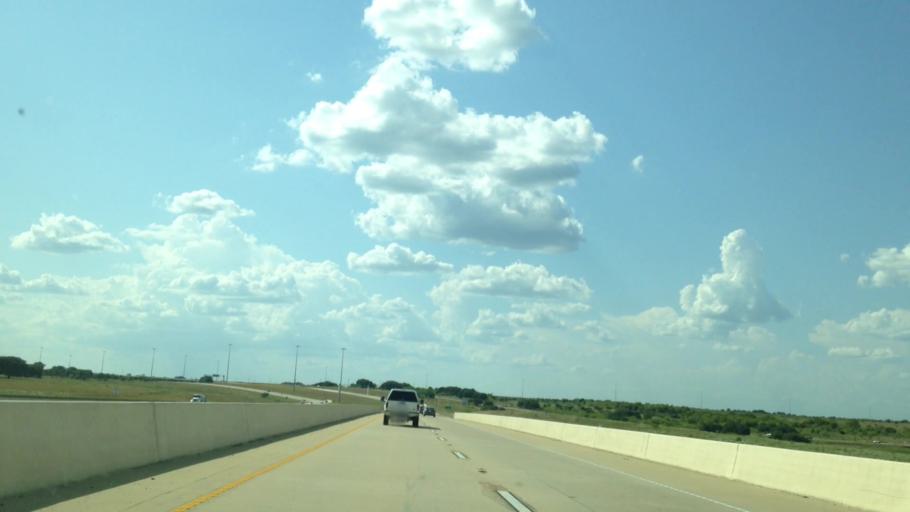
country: US
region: Texas
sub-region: Travis County
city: Onion Creek
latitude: 30.1068
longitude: -97.7891
